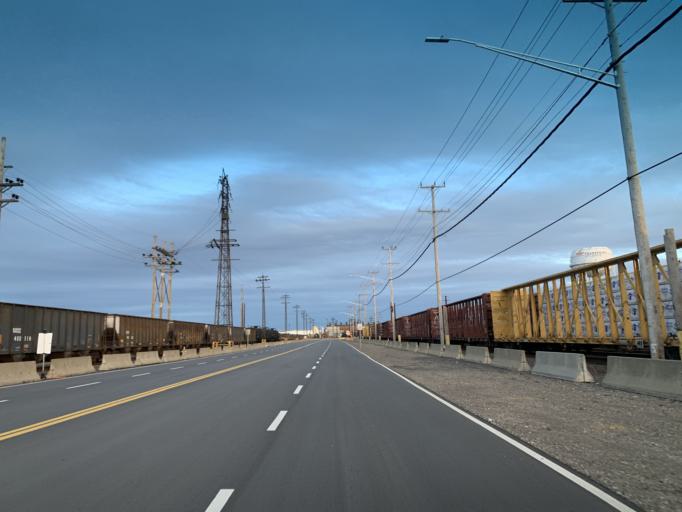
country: US
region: Maryland
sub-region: Baltimore County
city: Edgemere
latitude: 39.2264
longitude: -76.4863
